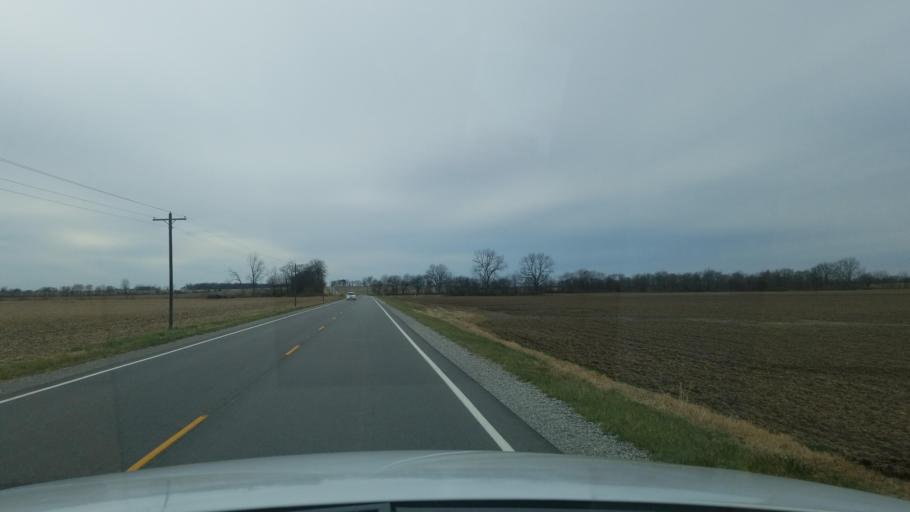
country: US
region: Illinois
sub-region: White County
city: Norris City
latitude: 37.9079
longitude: -88.1769
